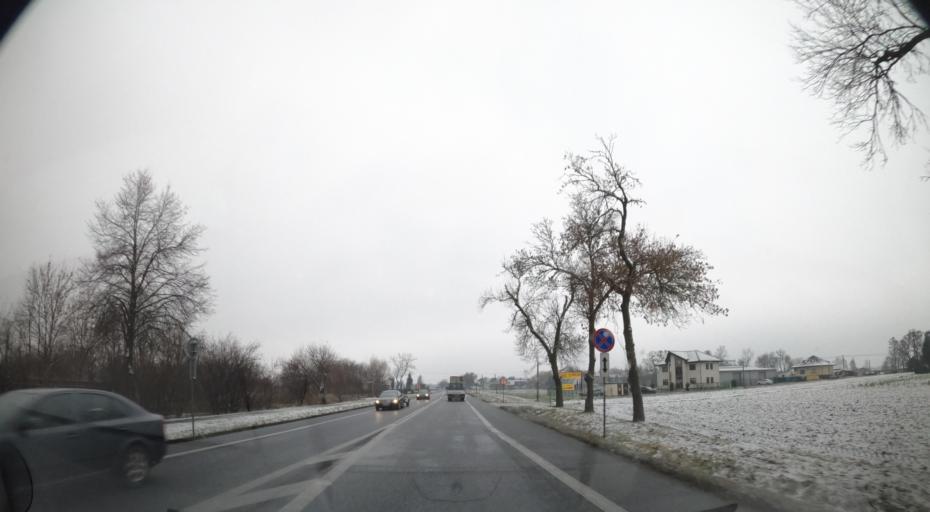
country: PL
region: Masovian Voivodeship
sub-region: Powiat warszawski zachodni
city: Bieniewice
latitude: 52.2038
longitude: 20.5183
